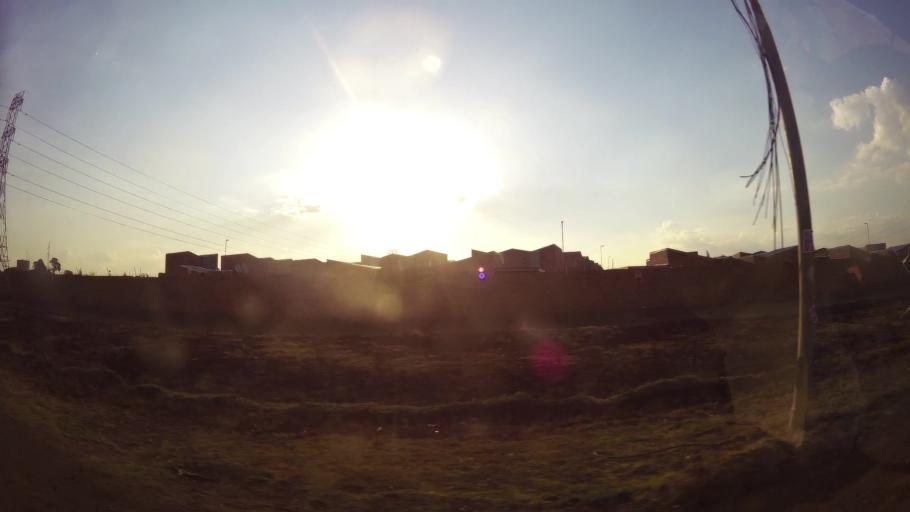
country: ZA
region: Gauteng
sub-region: Ekurhuleni Metropolitan Municipality
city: Boksburg
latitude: -26.3062
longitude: 28.2626
